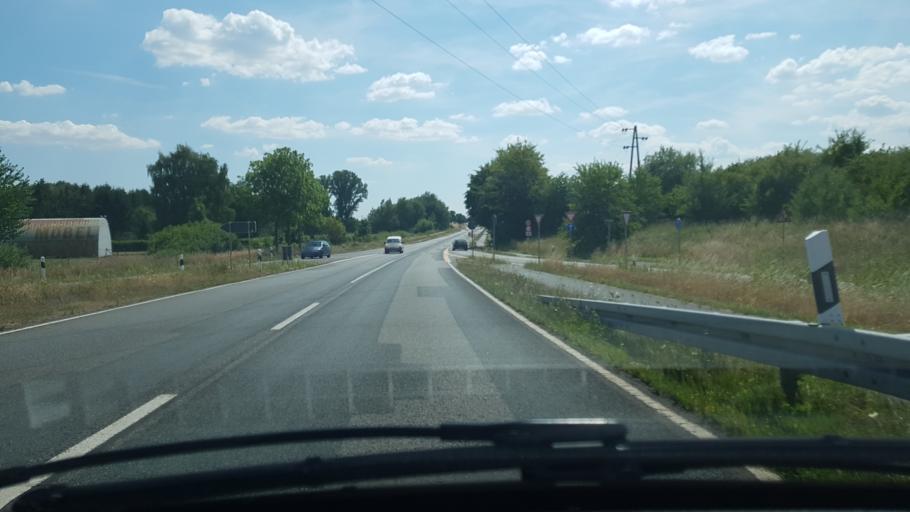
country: DE
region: Lower Saxony
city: Lehre
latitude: 52.3563
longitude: 10.6963
